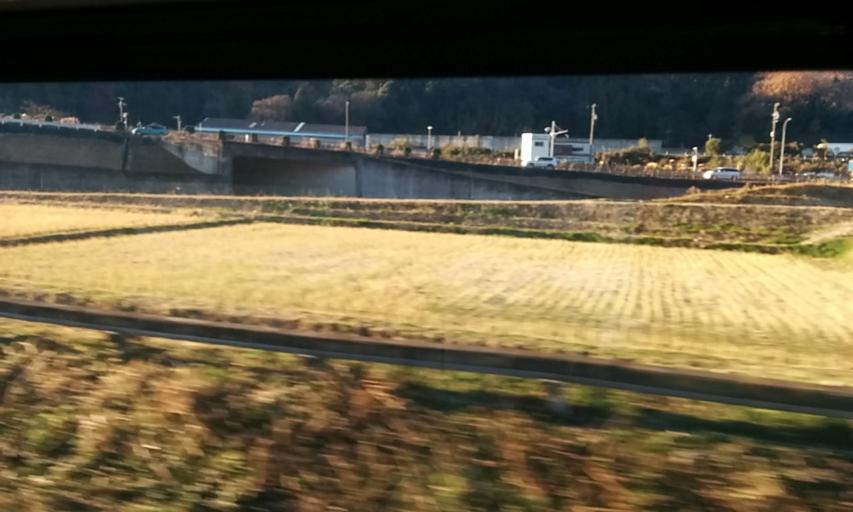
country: JP
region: Gifu
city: Mizunami
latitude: 35.3899
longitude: 137.2731
